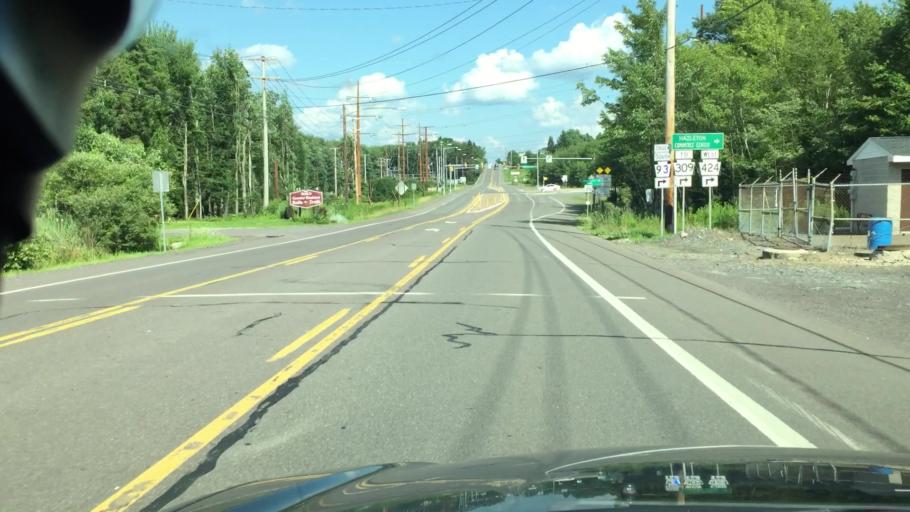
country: US
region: Pennsylvania
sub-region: Luzerne County
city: Hazleton
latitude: 40.9406
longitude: -75.9481
